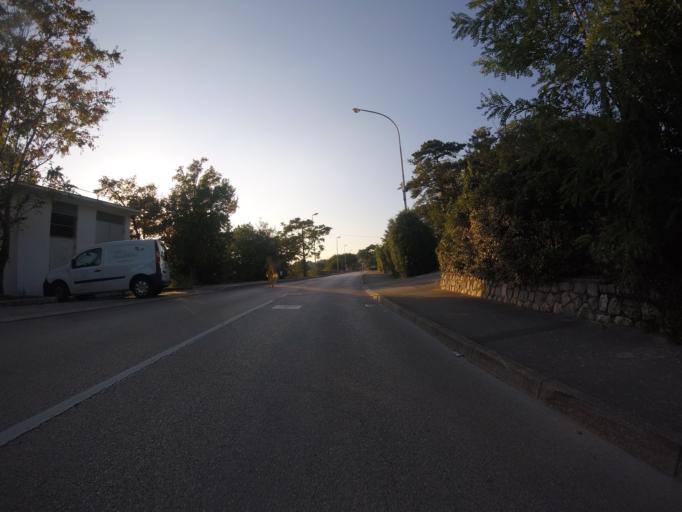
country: HR
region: Primorsko-Goranska
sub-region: Grad Crikvenica
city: Crikvenica
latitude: 45.1873
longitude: 14.6758
